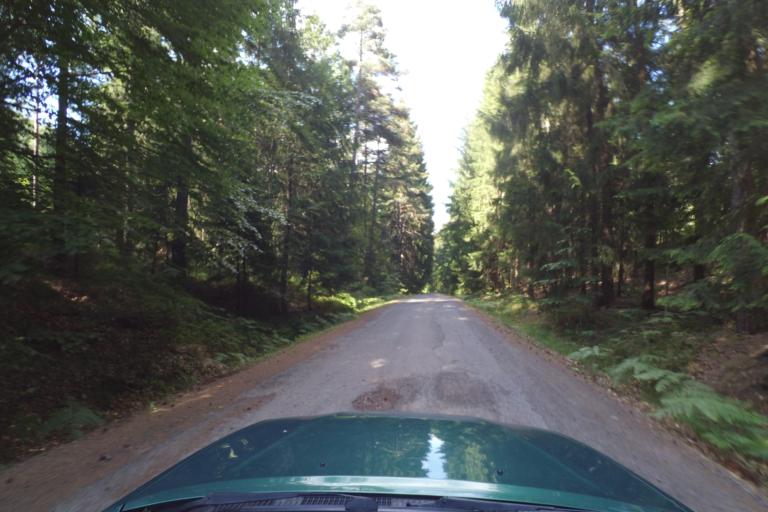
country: CZ
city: Osecna
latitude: 50.6808
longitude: 14.8972
